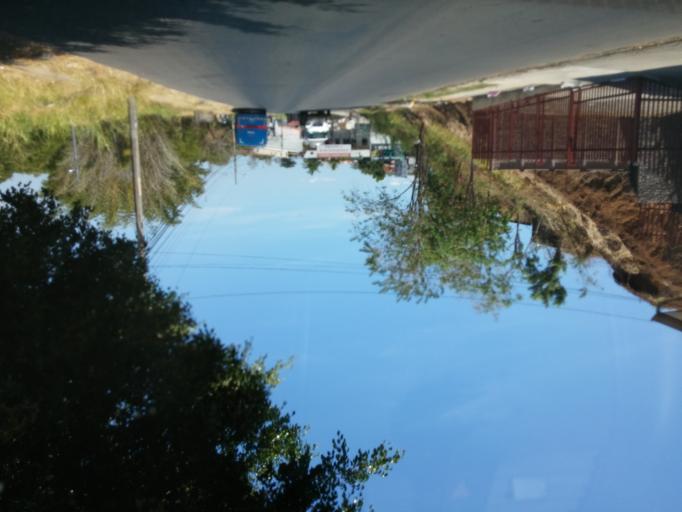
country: CR
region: Alajuela
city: Alajuela
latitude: 10.0180
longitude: -84.2220
